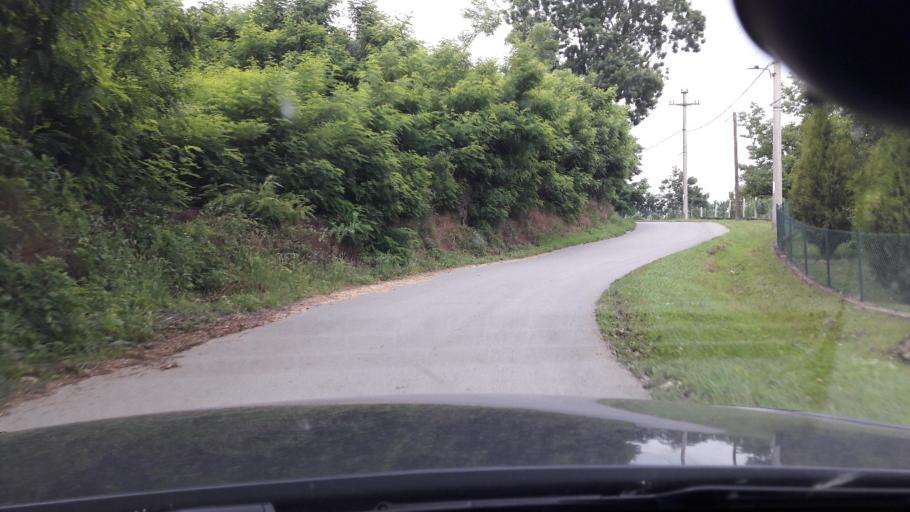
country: RS
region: Central Serbia
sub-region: Belgrade
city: Grocka
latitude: 44.6493
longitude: 20.6017
